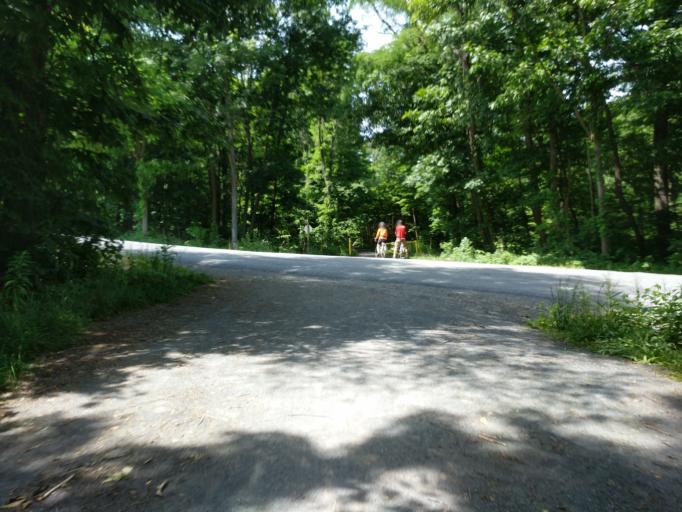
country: US
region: New York
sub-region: Tompkins County
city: Northwest Ithaca
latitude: 42.4925
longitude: -76.5414
